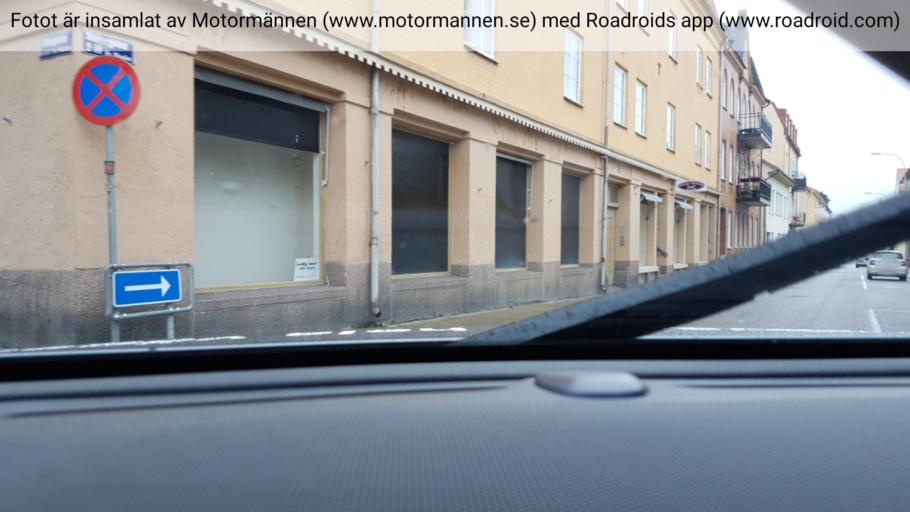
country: SE
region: Vaestra Goetaland
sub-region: Vanersborgs Kommun
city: Vanersborg
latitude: 58.3787
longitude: 12.3219
